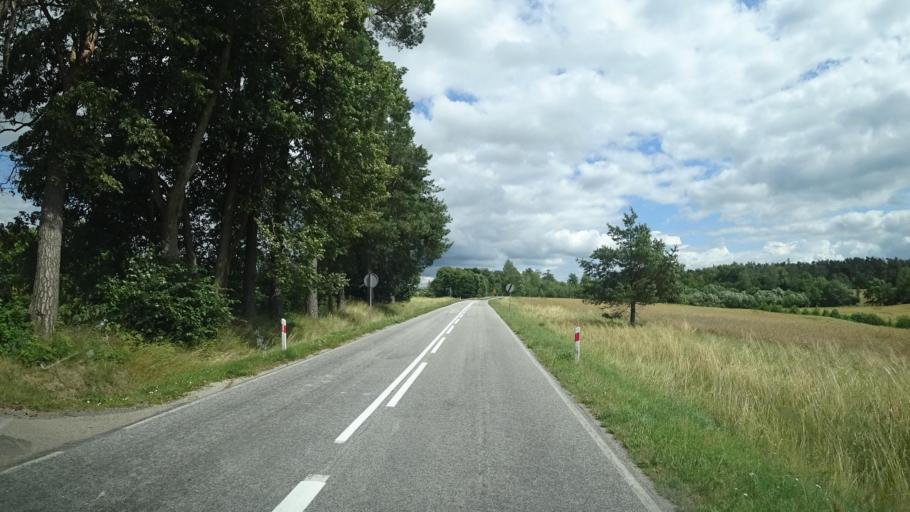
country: PL
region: Warmian-Masurian Voivodeship
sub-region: Powiat goldapski
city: Banie Mazurskie
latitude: 54.2125
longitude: 22.1709
